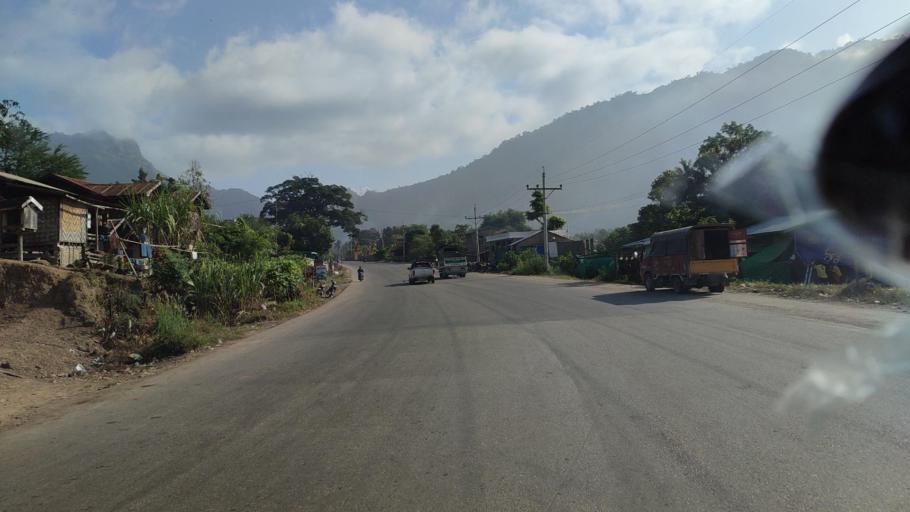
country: MM
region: Mandalay
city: Yamethin
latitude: 20.8172
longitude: 96.3934
